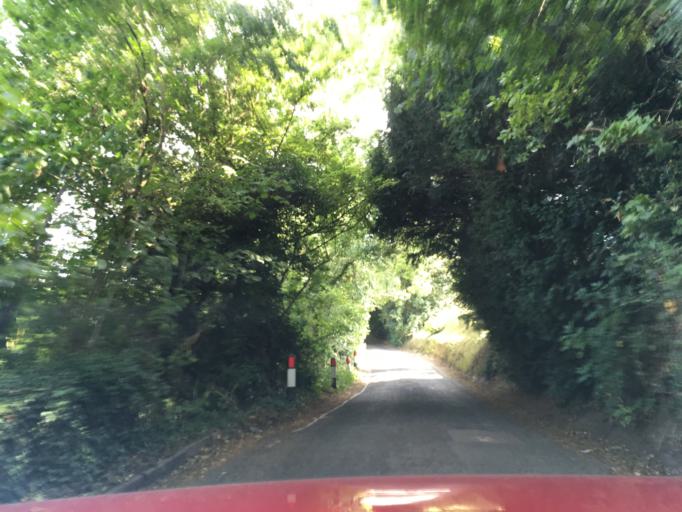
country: GB
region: England
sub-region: Kent
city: Maidstone
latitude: 51.2432
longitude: 0.5113
